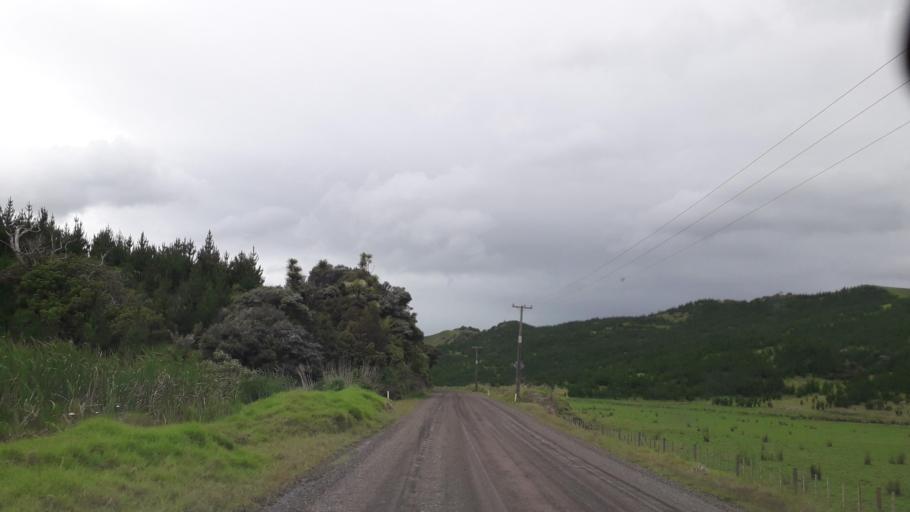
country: NZ
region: Northland
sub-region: Far North District
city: Ahipara
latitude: -35.4308
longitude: 173.3491
